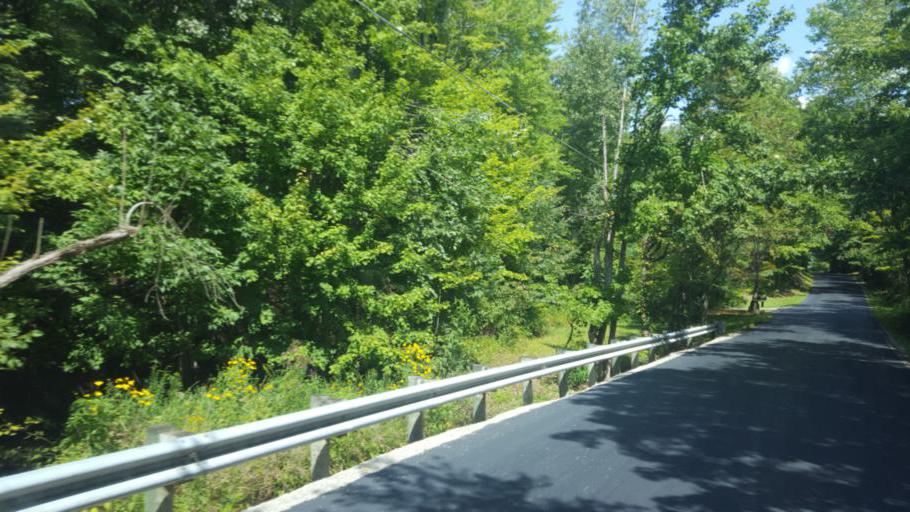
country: US
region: Ohio
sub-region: Delaware County
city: Lewis Center
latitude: 40.2517
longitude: -82.9524
